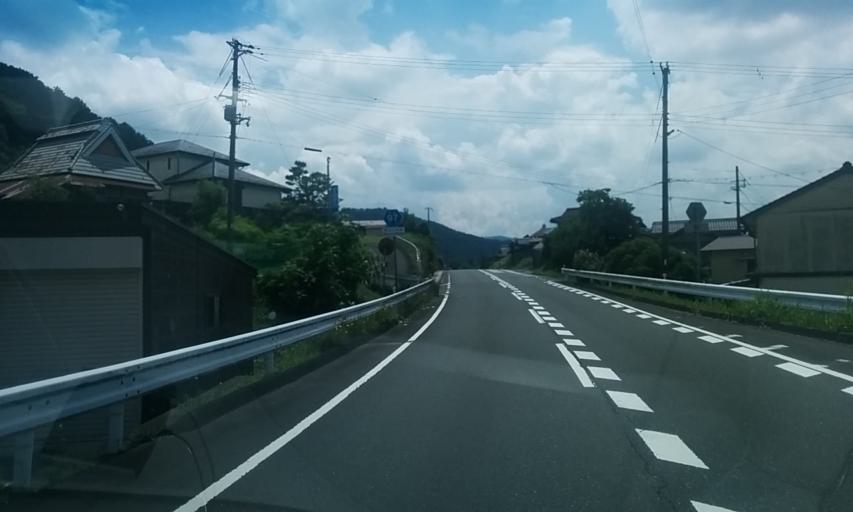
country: JP
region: Kyoto
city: Ayabe
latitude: 35.2017
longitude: 135.2601
